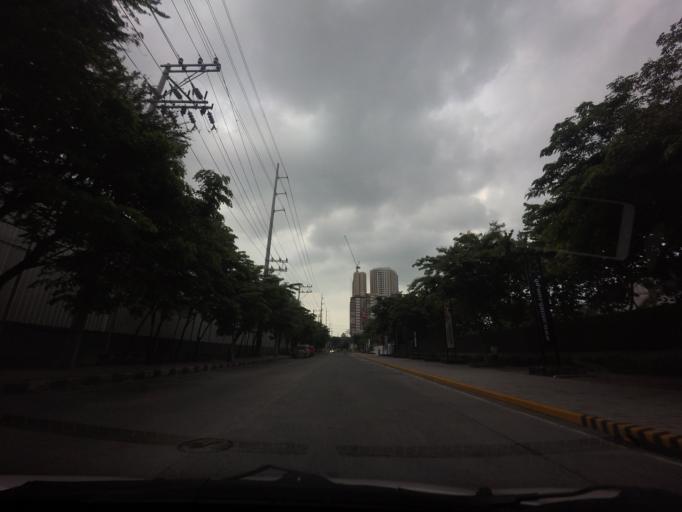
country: PH
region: Metro Manila
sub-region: Pasig
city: Pasig City
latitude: 14.5756
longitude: 121.0568
